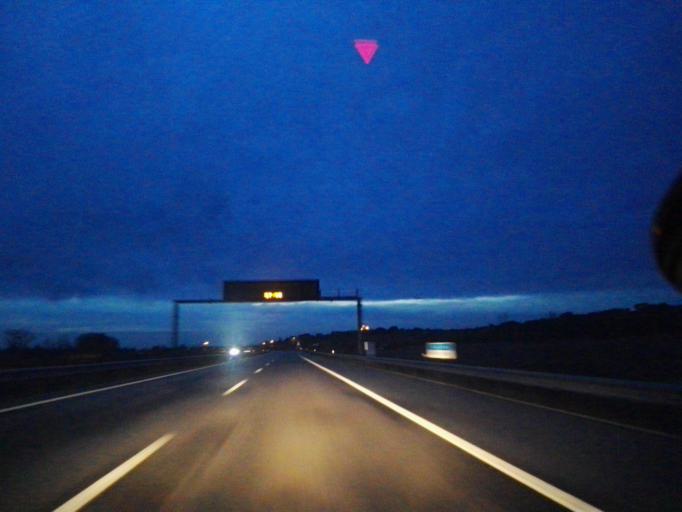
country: PT
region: Evora
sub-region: Estremoz
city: Estremoz
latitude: 38.8197
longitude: -7.5644
